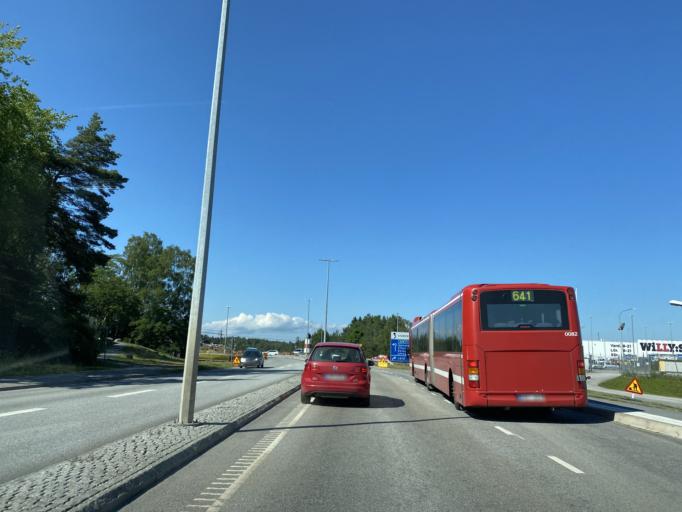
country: SE
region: Stockholm
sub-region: Norrtalje Kommun
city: Norrtalje
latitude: 59.7651
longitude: 18.6915
